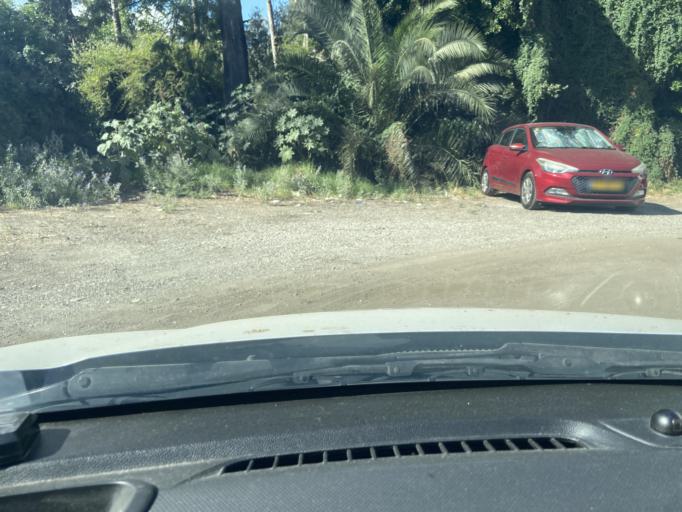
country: IL
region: Central District
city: Yehud
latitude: 32.0311
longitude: 34.8934
